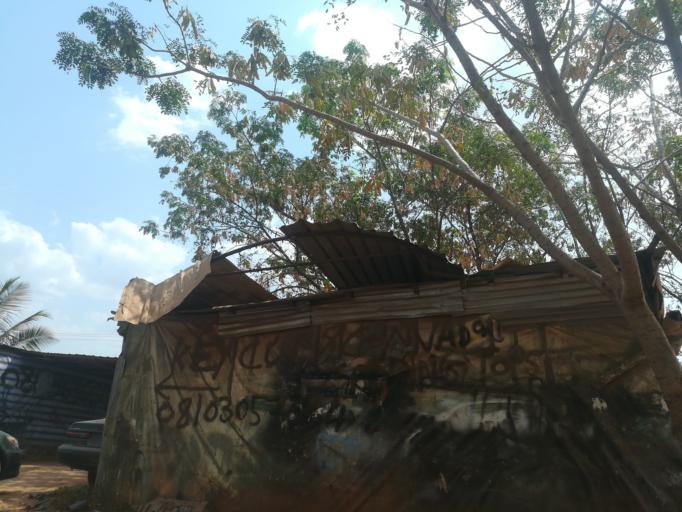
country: NG
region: Abuja Federal Capital Territory
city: Abuja
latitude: 9.0598
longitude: 7.4515
